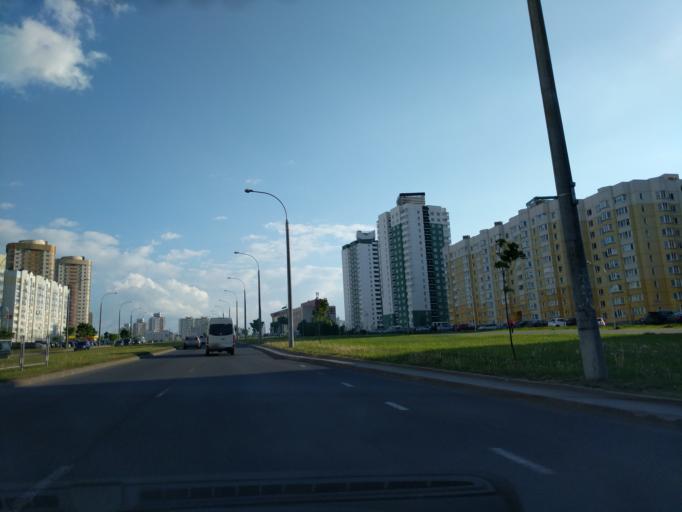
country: BY
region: Minsk
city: Zhdanovichy
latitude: 53.9237
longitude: 27.4396
